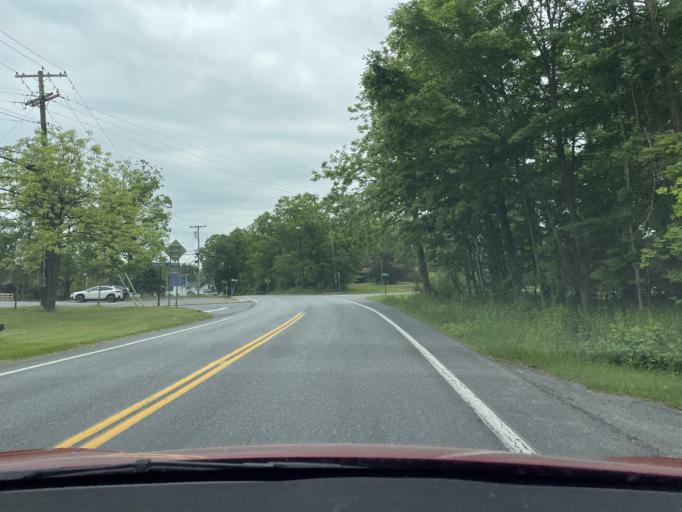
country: US
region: New York
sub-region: Ulster County
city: West Hurley
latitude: 42.0071
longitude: -74.1061
